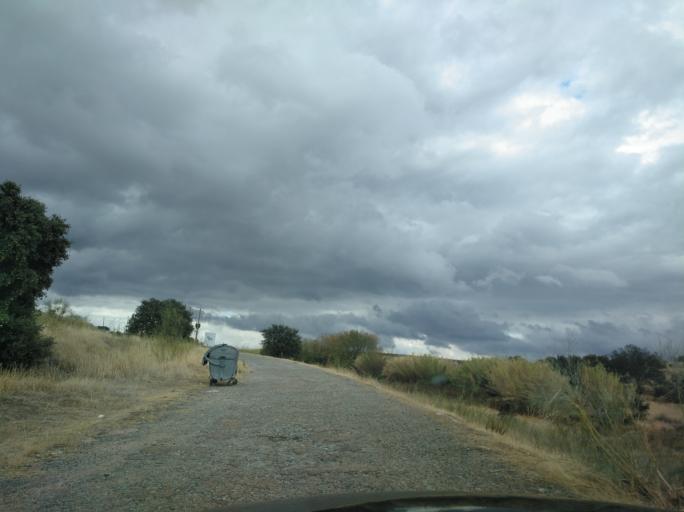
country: PT
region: Portalegre
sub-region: Campo Maior
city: Campo Maior
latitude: 39.0357
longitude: -7.1331
